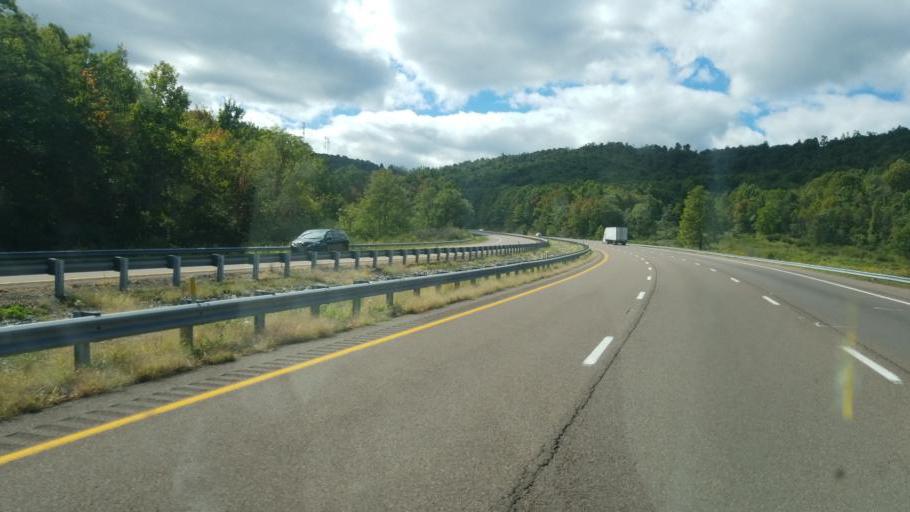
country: US
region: Maryland
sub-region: Allegany County
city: Cumberland
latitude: 39.7144
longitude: -78.6119
